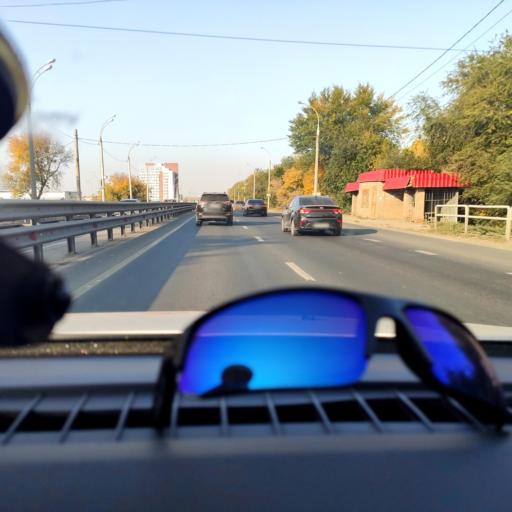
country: RU
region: Samara
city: Samara
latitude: 53.1115
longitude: 50.1652
